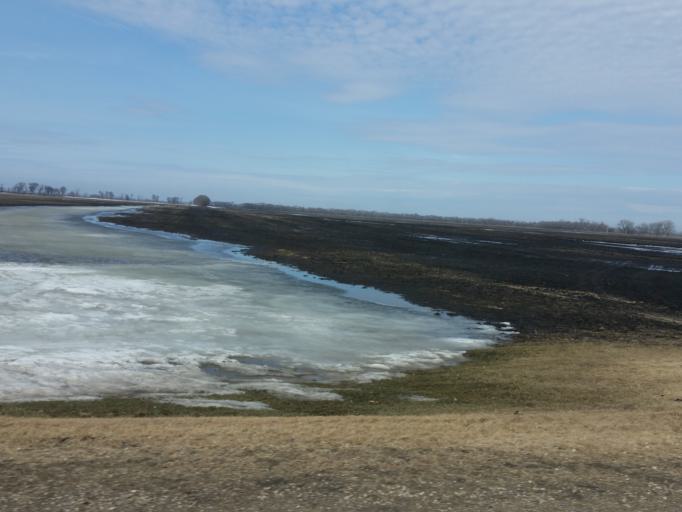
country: US
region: North Dakota
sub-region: Walsh County
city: Grafton
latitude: 48.4266
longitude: -97.2232
